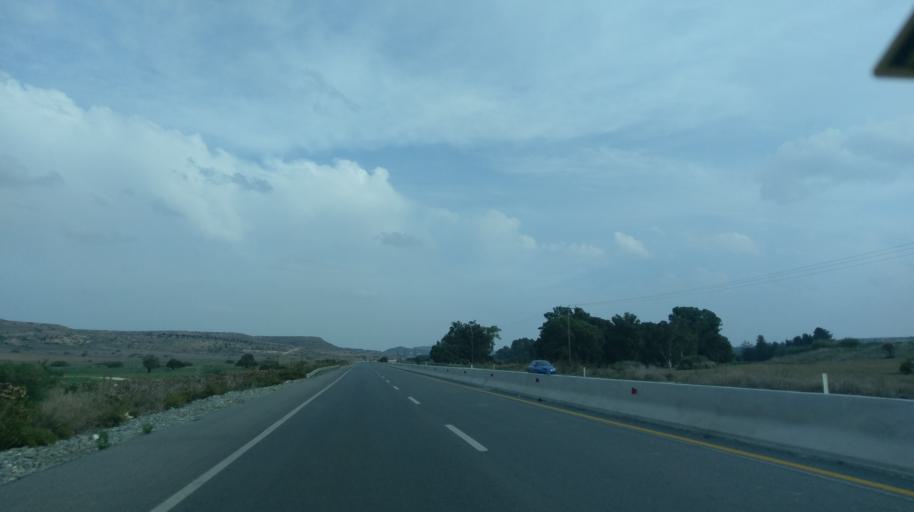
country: CY
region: Lefkosia
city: Peristerona
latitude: 35.1959
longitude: 33.0884
